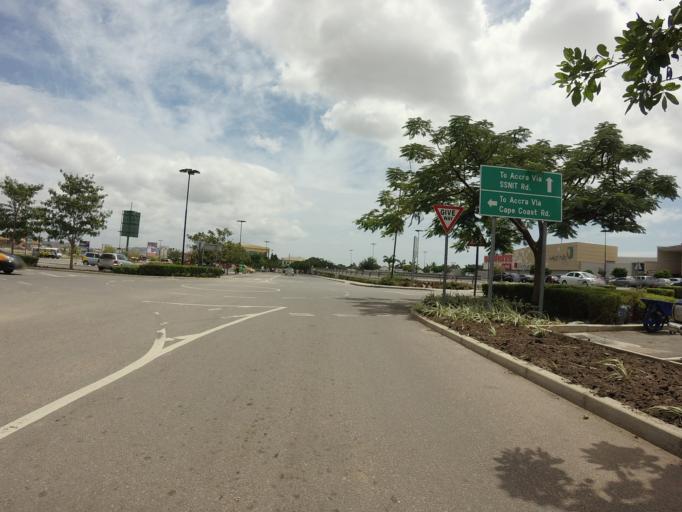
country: GH
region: Greater Accra
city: Gbawe
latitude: 5.5452
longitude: -0.3434
